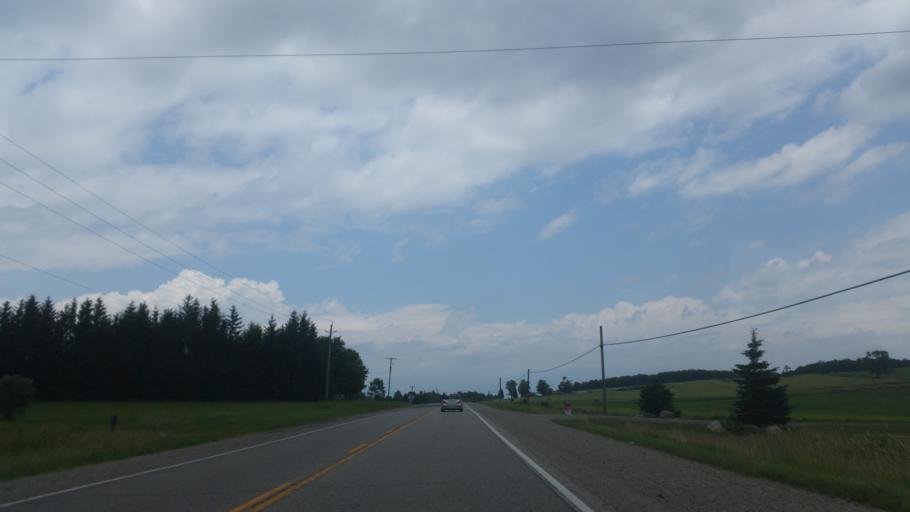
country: CA
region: Ontario
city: Orangeville
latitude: 43.7240
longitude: -80.1057
